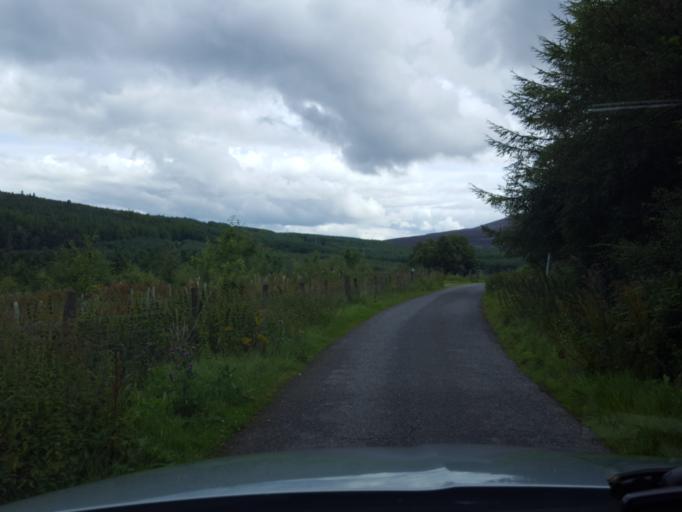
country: GB
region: Scotland
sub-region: Highland
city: Grantown on Spey
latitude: 57.3358
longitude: -3.5129
